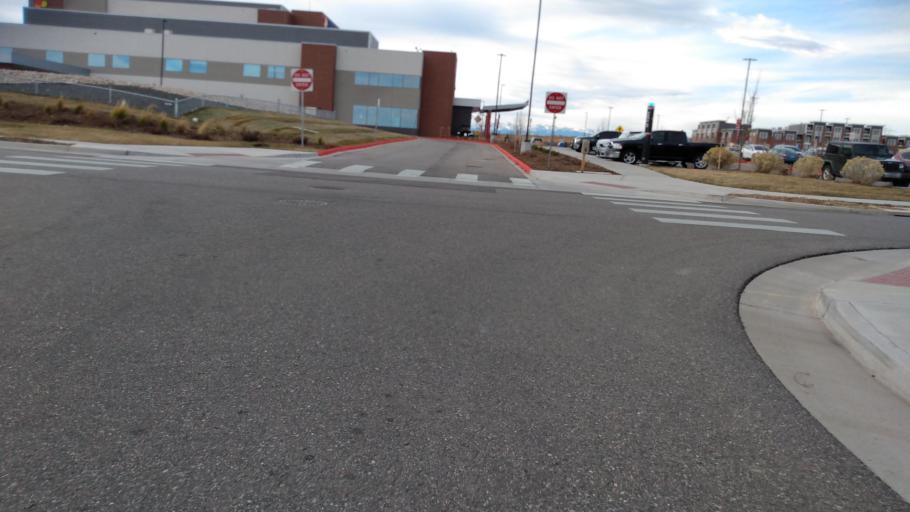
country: US
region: Colorado
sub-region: Boulder County
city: Erie
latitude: 40.0023
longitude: -104.9919
